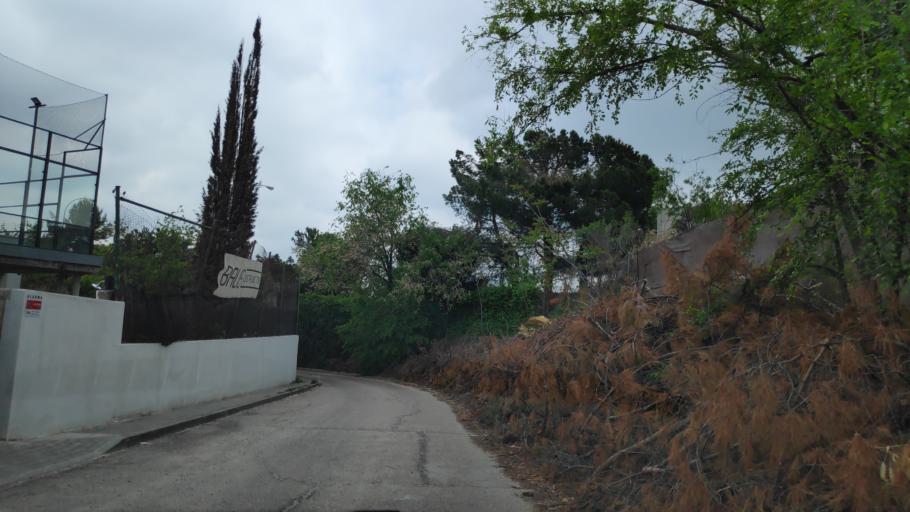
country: ES
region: Madrid
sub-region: Provincia de Madrid
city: Pozuelo de Alarcon
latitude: 40.4639
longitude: -3.7910
